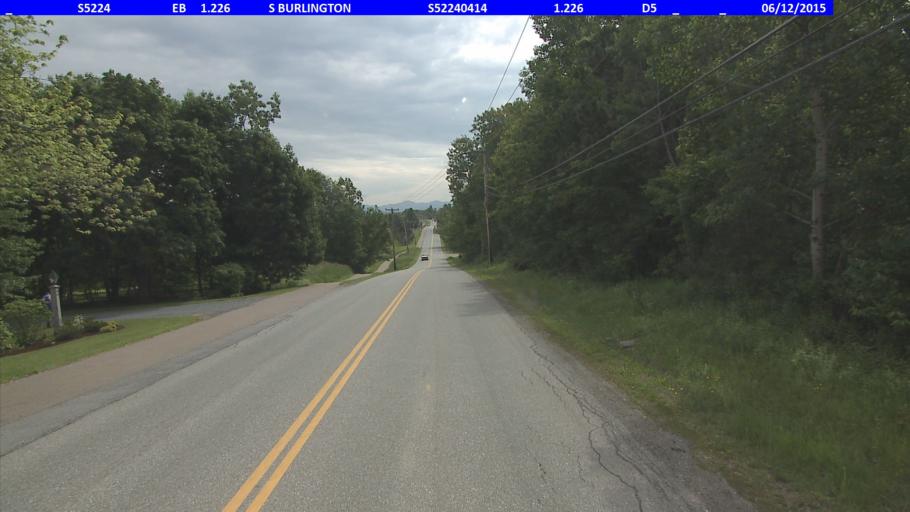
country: US
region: Vermont
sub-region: Chittenden County
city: South Burlington
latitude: 44.4423
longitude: -73.1856
